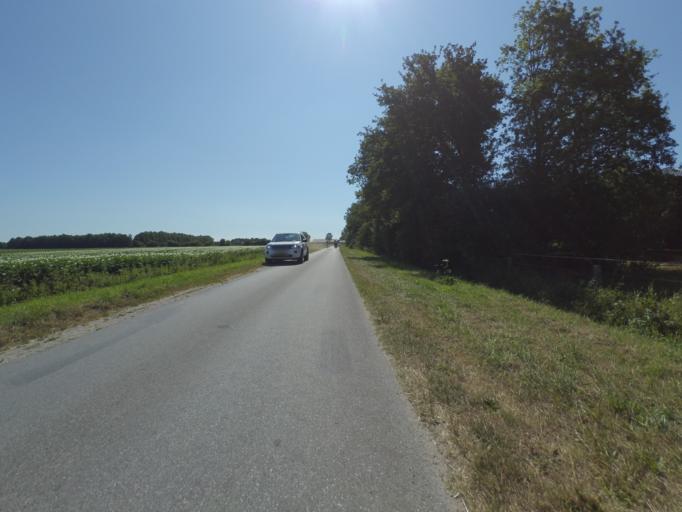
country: NL
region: Drenthe
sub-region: Gemeente Aa en Hunze
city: Anloo
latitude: 52.9781
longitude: 6.6717
